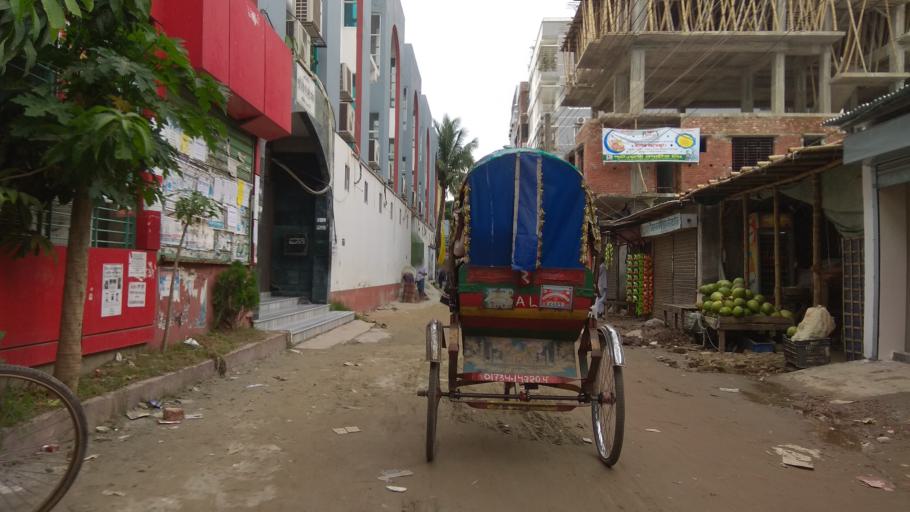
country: BD
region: Dhaka
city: Tungi
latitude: 23.8235
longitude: 90.3542
